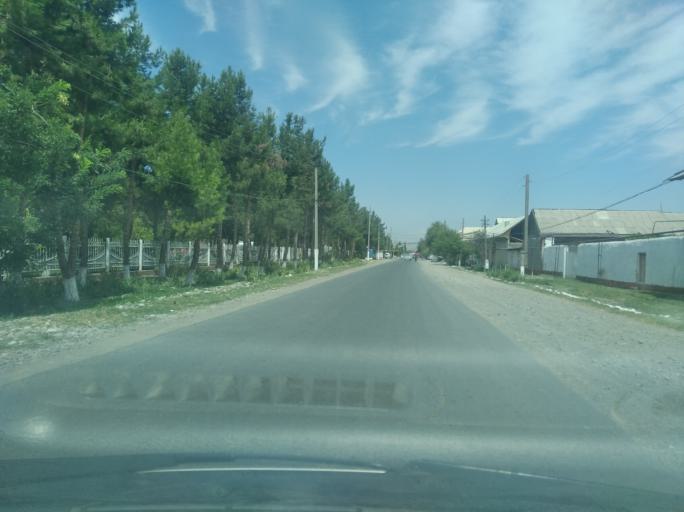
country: KG
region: Osh
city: Aravan
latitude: 40.6113
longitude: 72.4567
